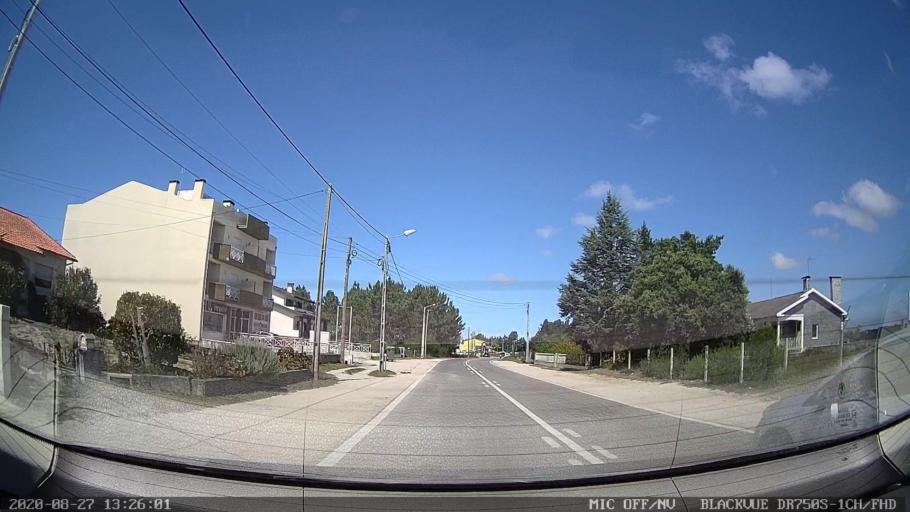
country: PT
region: Aveiro
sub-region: Vagos
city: Vagos
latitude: 40.5412
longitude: -8.6775
